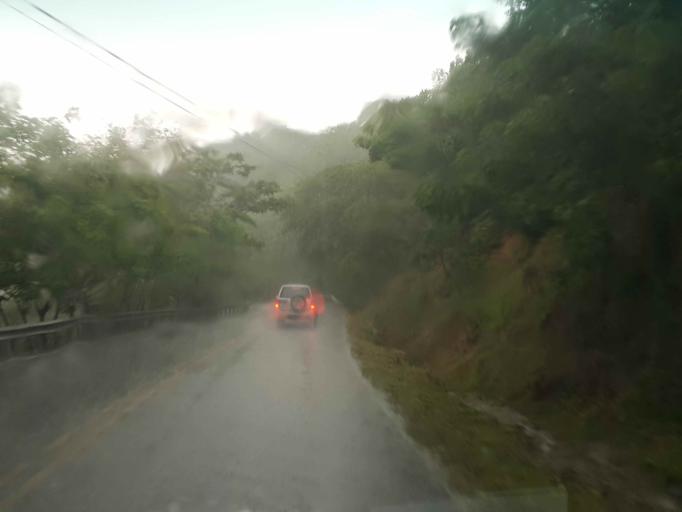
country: CR
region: Puntarenas
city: Miramar
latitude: 10.1312
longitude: -84.8332
